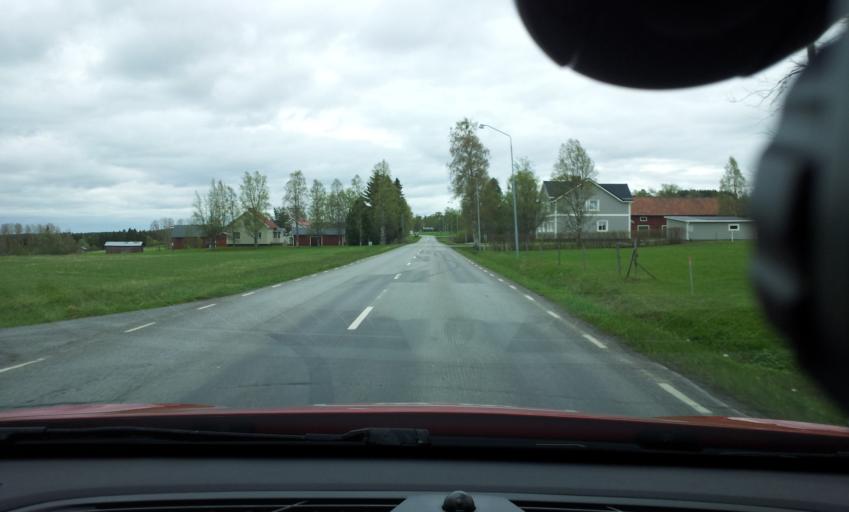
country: SE
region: Jaemtland
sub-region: OEstersunds Kommun
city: Brunflo
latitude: 63.0944
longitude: 14.7463
